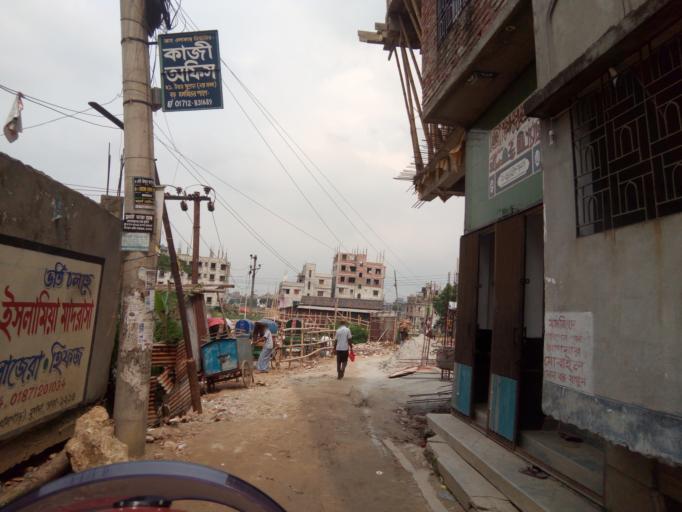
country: BD
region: Dhaka
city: Paltan
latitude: 23.7335
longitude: 90.4357
